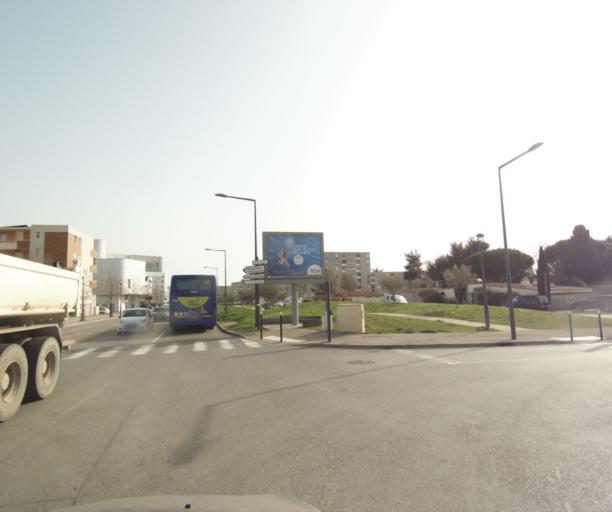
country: FR
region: Provence-Alpes-Cote d'Azur
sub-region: Departement des Bouches-du-Rhone
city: Vitrolles
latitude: 43.4441
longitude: 5.2516
